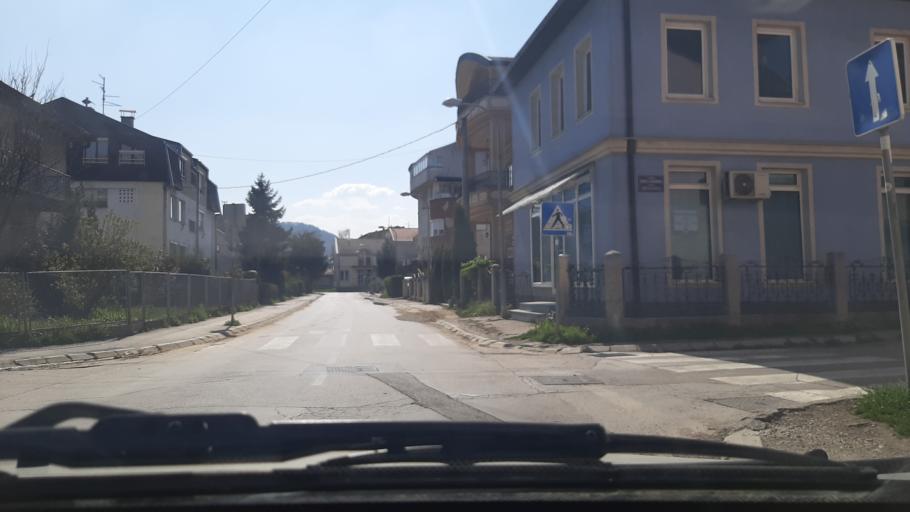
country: BA
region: Republika Srpska
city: Banja Luka
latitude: 44.7687
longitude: 17.1834
